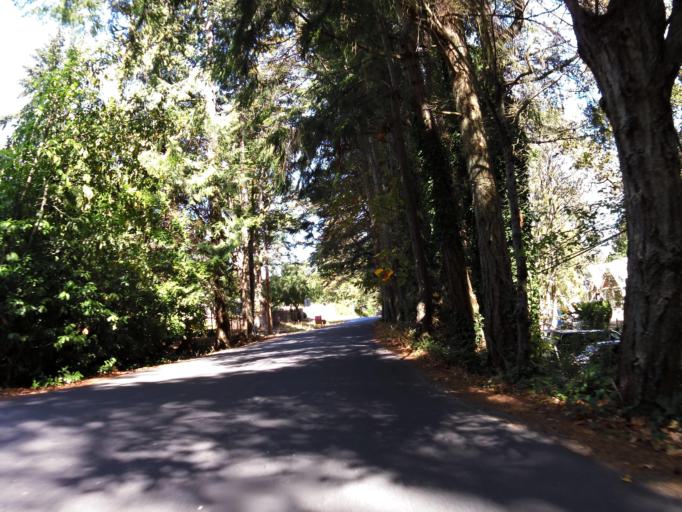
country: CA
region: British Columbia
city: Victoria
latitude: 48.5252
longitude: -123.3727
